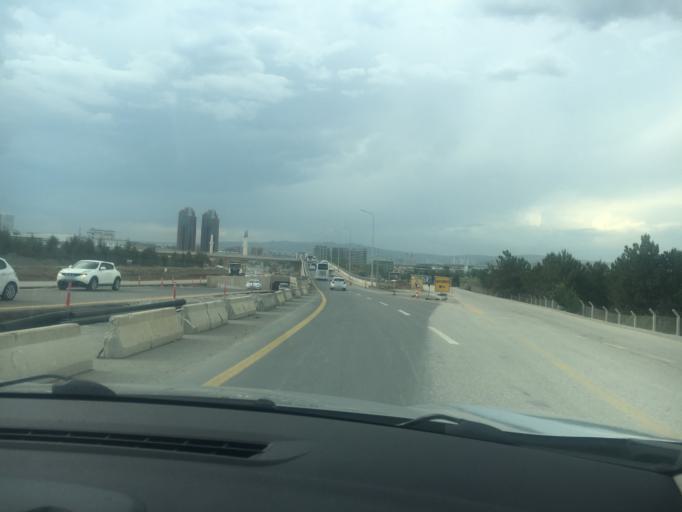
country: TR
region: Ankara
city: Batikent
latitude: 39.8976
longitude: 32.7668
